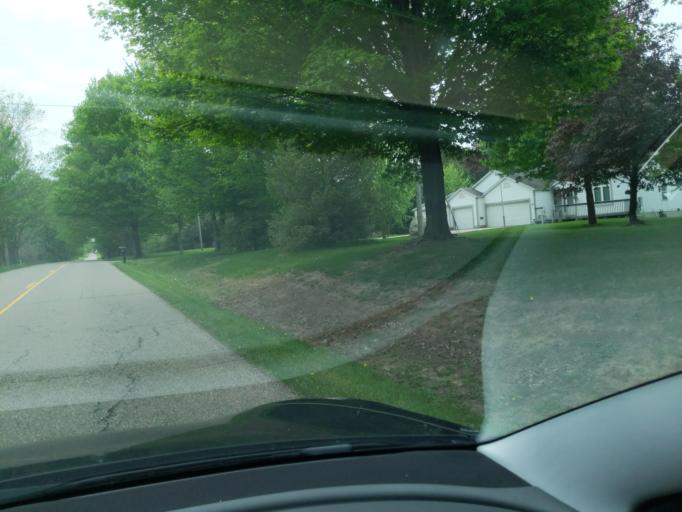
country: US
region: Michigan
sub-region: Ingham County
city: Holt
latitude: 42.5583
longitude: -84.5424
